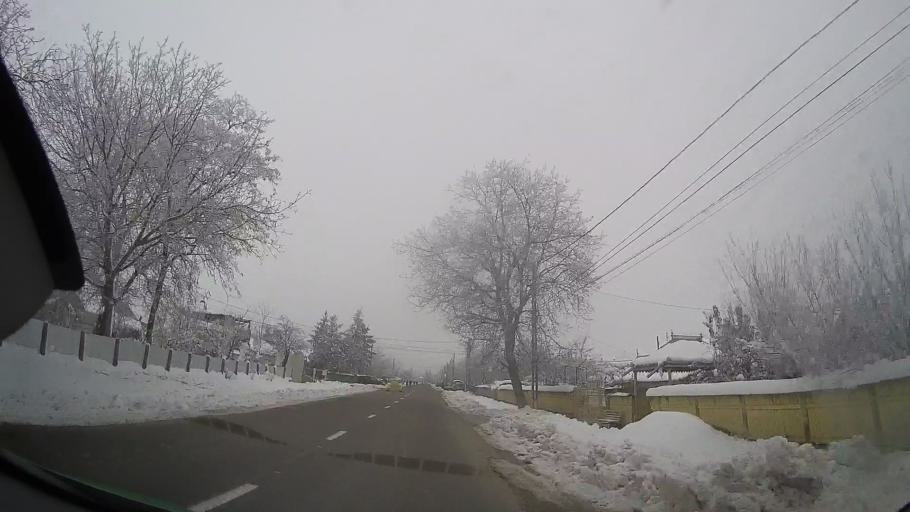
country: RO
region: Neamt
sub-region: Comuna Horia
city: Cotu Vames
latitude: 46.9008
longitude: 26.9554
